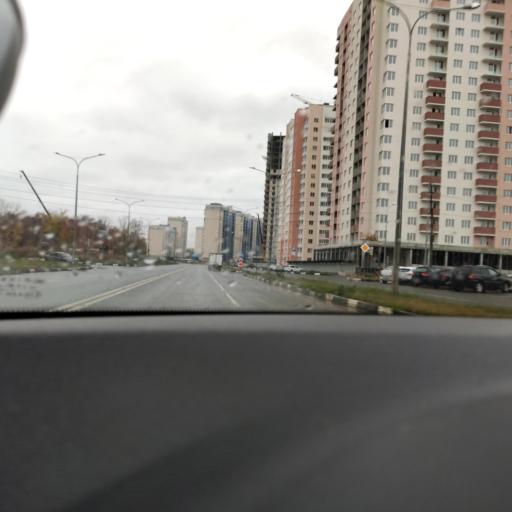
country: RU
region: Samara
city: Samara
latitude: 53.1456
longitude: 50.0760
